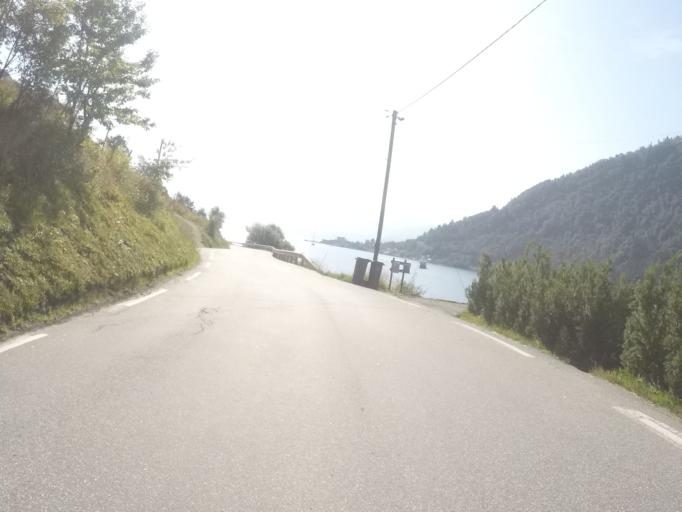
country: NO
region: Sogn og Fjordane
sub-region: Balestrand
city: Balestrand
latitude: 61.2199
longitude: 6.5040
